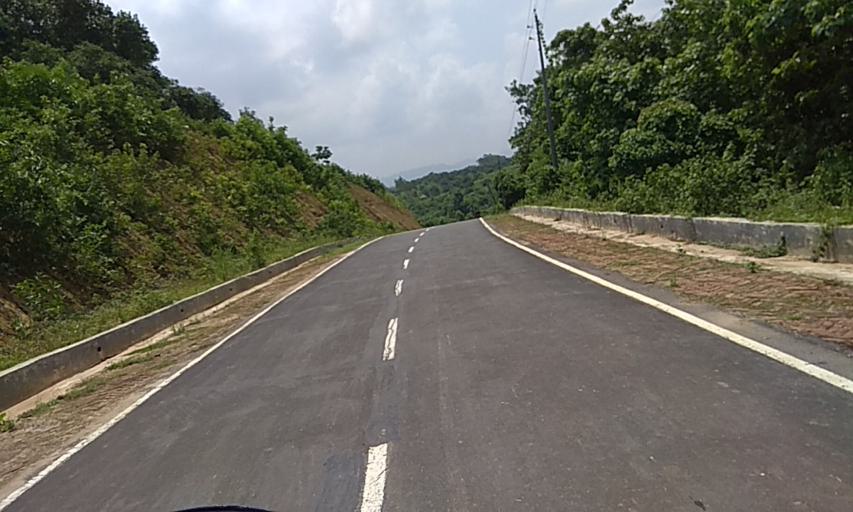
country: BD
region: Chittagong
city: Manikchari
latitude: 22.9386
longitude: 91.9034
